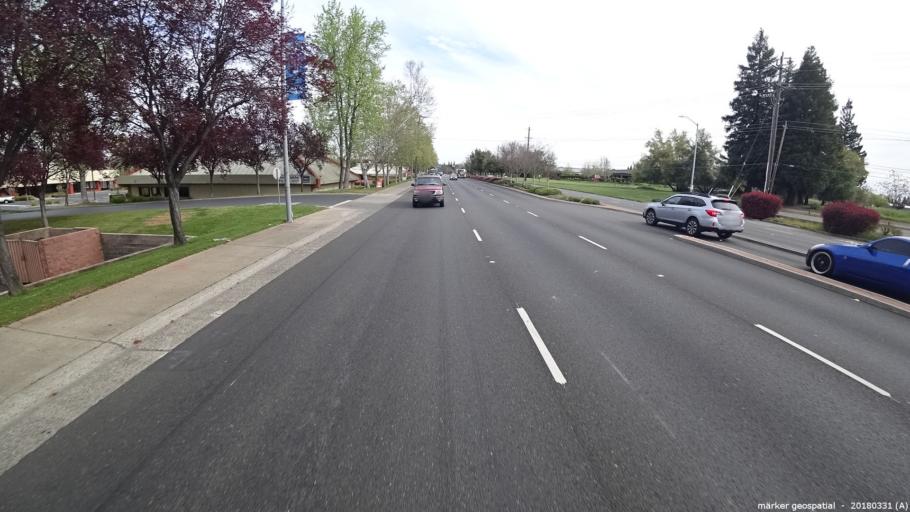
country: US
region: California
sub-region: Sacramento County
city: Gold River
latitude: 38.6208
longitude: -121.2675
